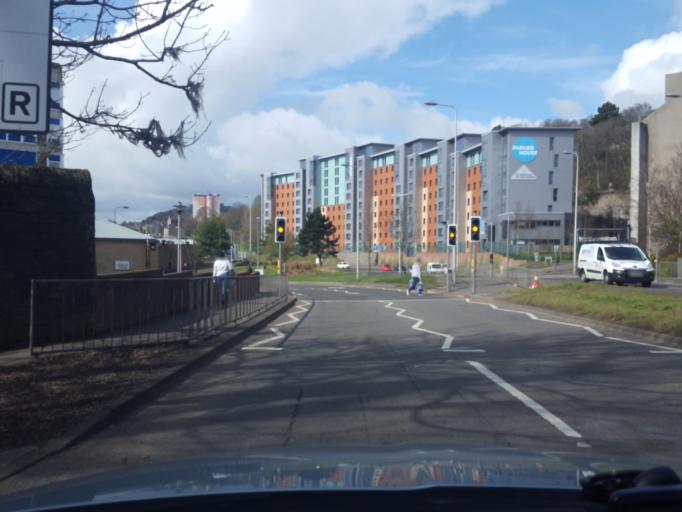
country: GB
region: Scotland
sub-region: Dundee City
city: Dundee
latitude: 56.4636
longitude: -2.9774
